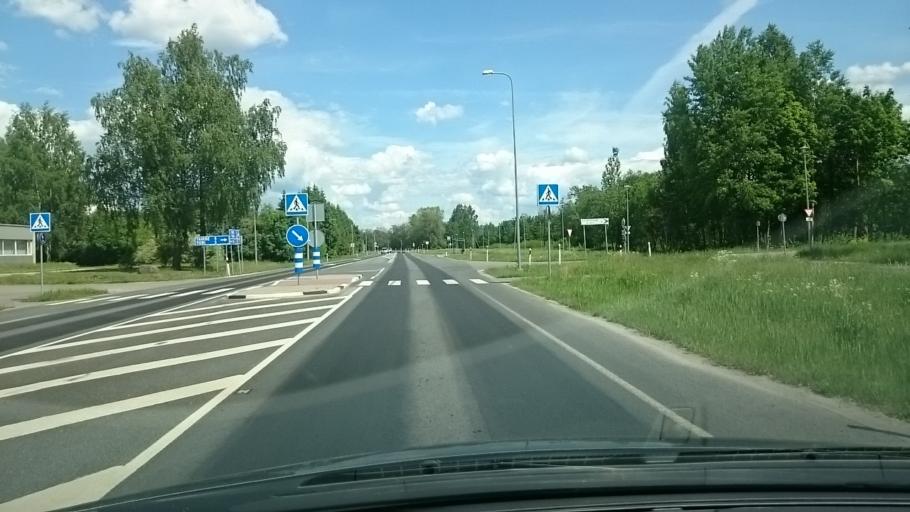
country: EE
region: Jaervamaa
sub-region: Tueri vald
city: Tueri
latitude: 58.8244
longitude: 25.4498
